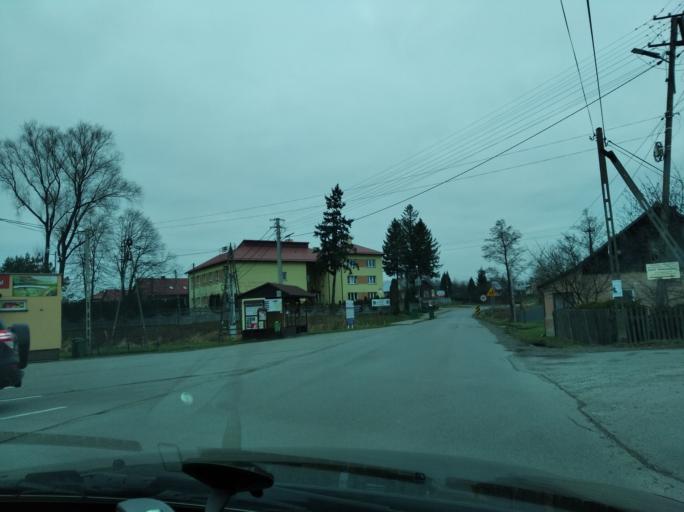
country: PL
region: Subcarpathian Voivodeship
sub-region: Powiat lancucki
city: Rakszawa
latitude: 50.1697
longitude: 22.2332
